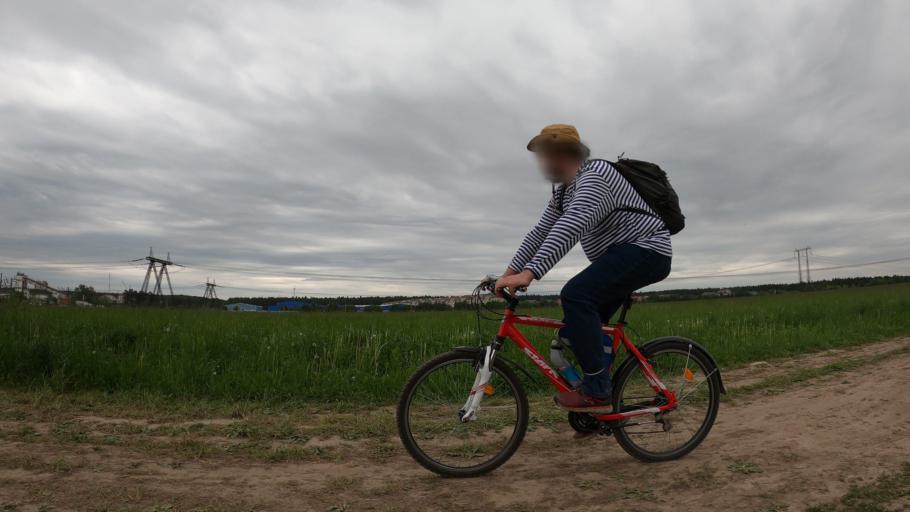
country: RU
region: Moskovskaya
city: Lesnyye Polyany
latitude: 55.9620
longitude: 37.8824
